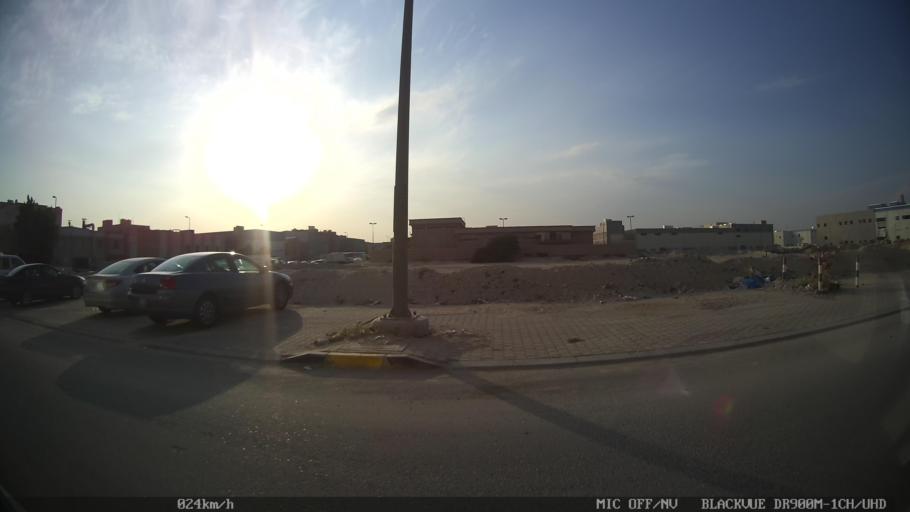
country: KW
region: Al Farwaniyah
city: Janub as Surrah
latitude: 29.2409
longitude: 48.0041
